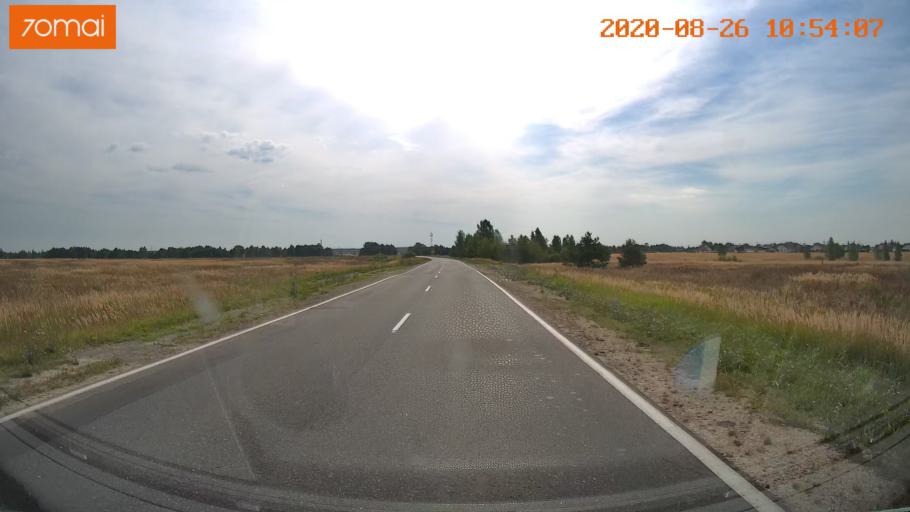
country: RU
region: Rjazan
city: Izhevskoye
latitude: 54.6321
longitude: 41.1568
